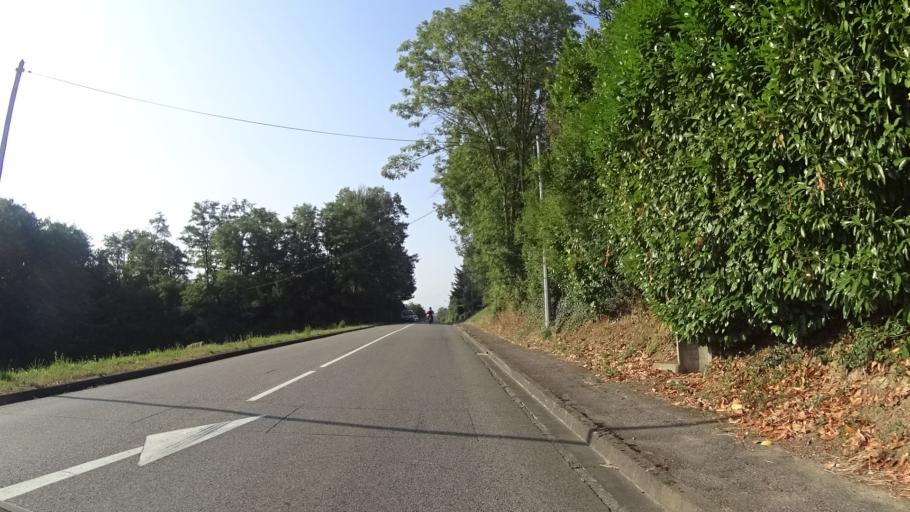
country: FR
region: Midi-Pyrenees
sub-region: Departement de l'Ariege
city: Mirepoix
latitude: 43.0786
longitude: 1.8768
